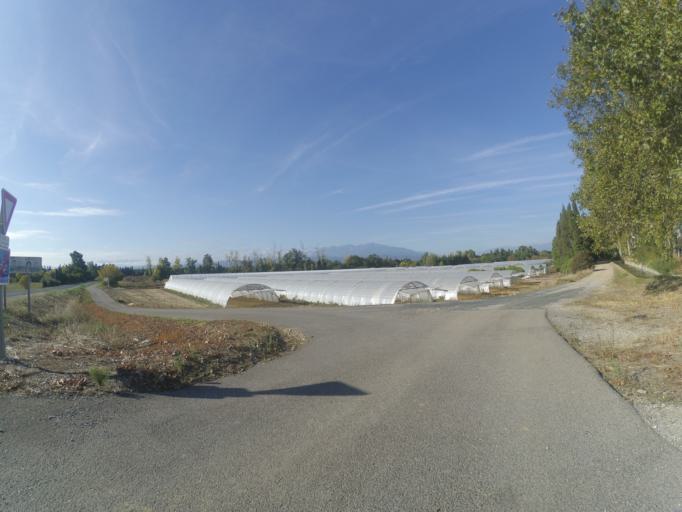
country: FR
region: Languedoc-Roussillon
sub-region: Departement des Pyrenees-Orientales
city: Pezilla-la-Riviere
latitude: 42.6960
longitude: 2.7576
